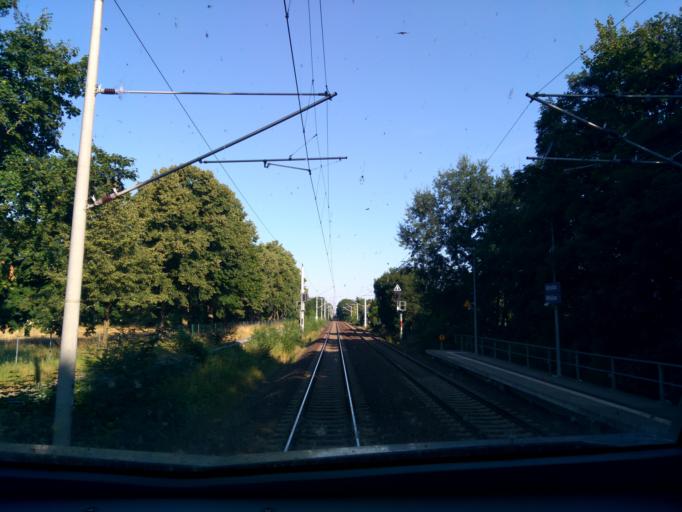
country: DE
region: Brandenburg
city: Vetschau
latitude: 51.7904
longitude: 14.0790
